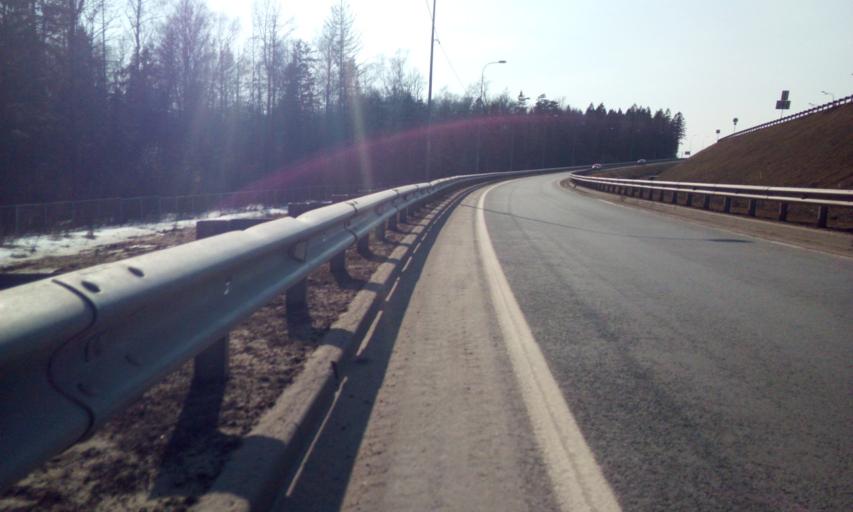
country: RU
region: Moskovskaya
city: Kokoshkino
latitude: 55.6236
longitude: 37.1738
